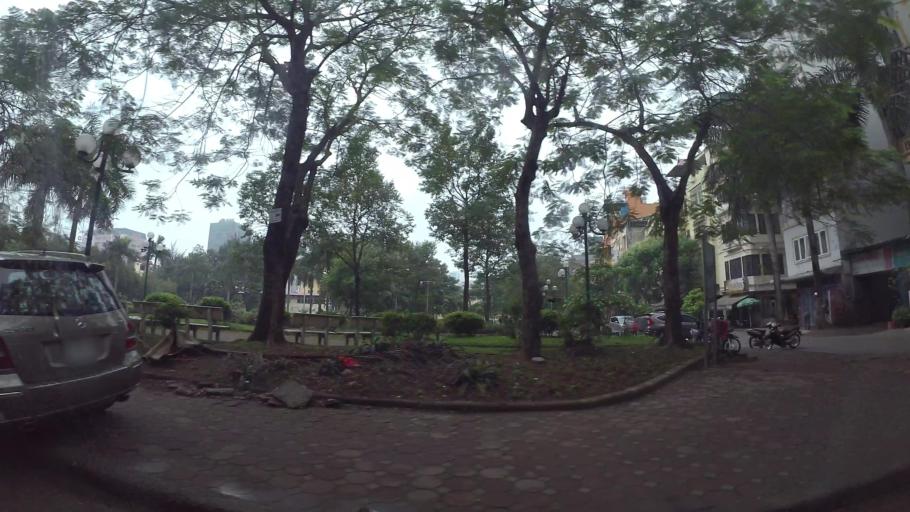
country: VN
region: Ha Noi
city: Dong Da
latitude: 21.0169
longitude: 105.8271
